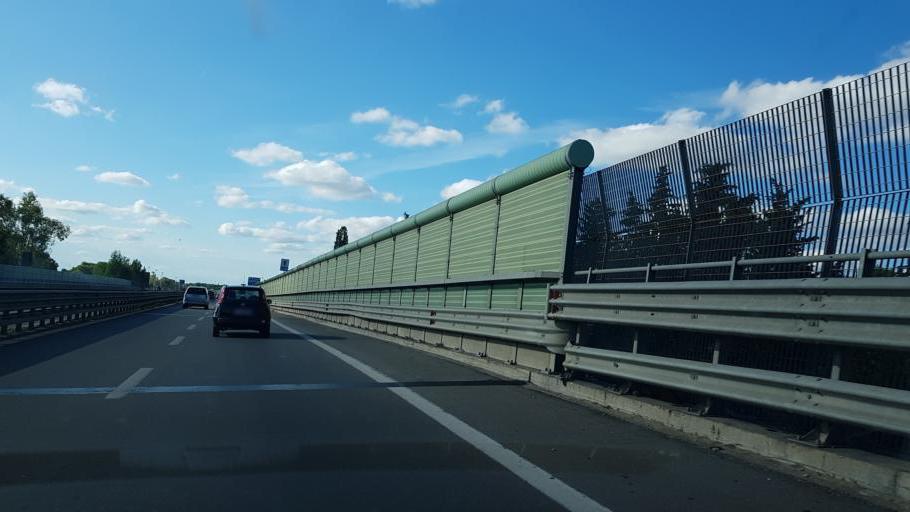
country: IT
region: Apulia
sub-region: Provincia di Lecce
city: Lequile
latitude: 40.3299
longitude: 18.1407
